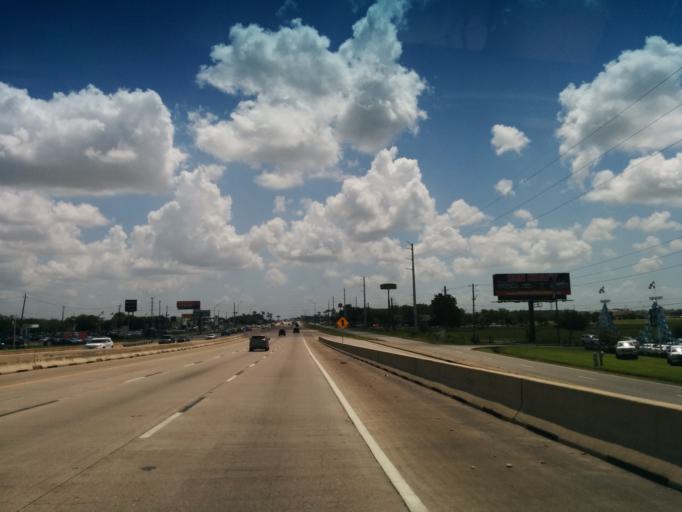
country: US
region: Texas
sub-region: Harris County
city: Highlands
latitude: 29.8025
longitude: -94.9947
